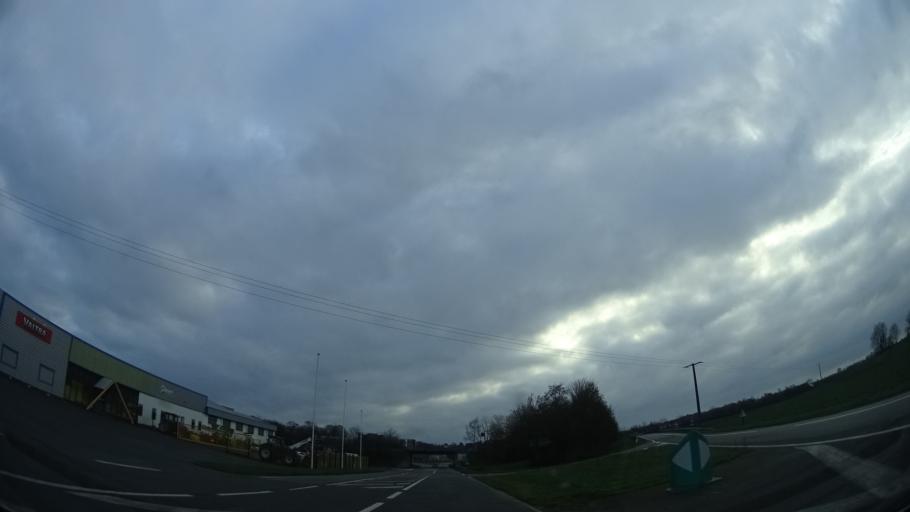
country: FR
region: Brittany
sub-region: Departement d'Ille-et-Vilaine
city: Poce-les-Bois
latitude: 48.1230
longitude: -1.2353
